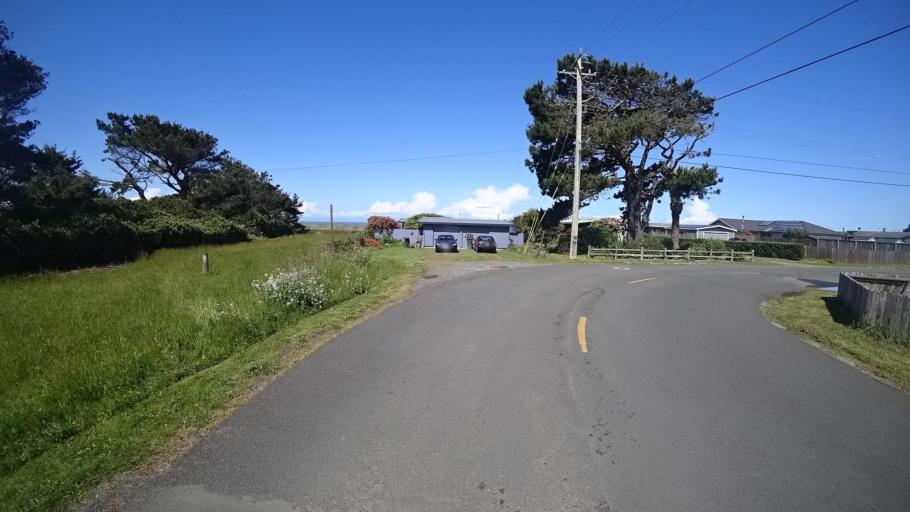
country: US
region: California
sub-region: Humboldt County
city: McKinleyville
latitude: 40.9380
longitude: -124.1273
